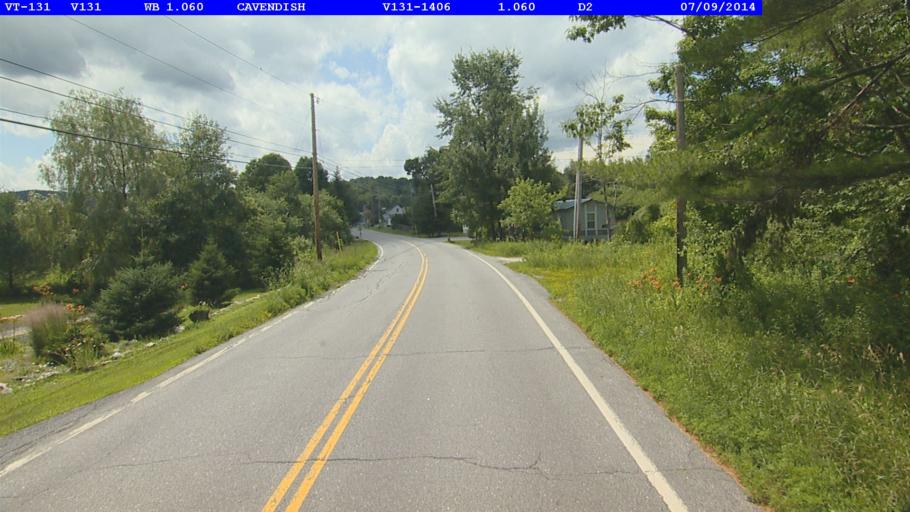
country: US
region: Vermont
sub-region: Windsor County
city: Chester
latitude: 43.3852
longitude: -72.6278
